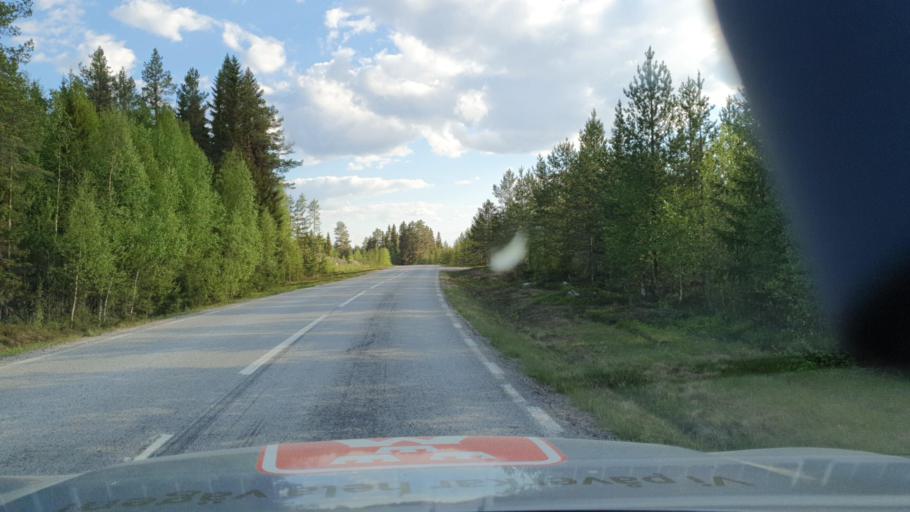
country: SE
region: Vaesterbotten
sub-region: Asele Kommun
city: Asele
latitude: 63.8585
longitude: 17.1662
